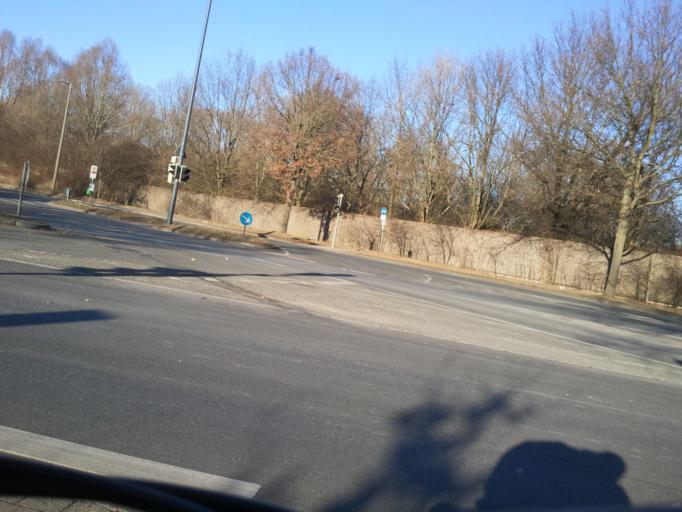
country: DE
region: Lower Saxony
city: Stuhr
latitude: 53.0811
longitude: 8.7554
